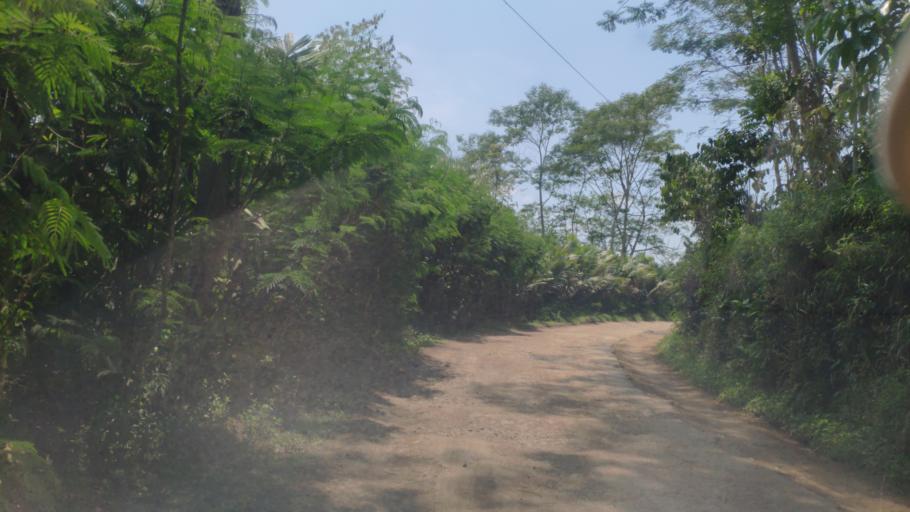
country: ID
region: Central Java
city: Wonosobo
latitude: -7.2817
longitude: 109.7368
